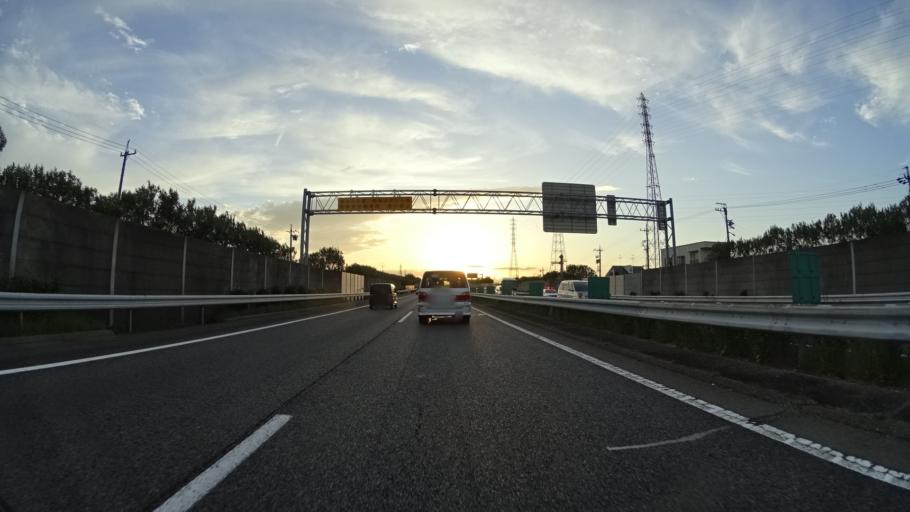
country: JP
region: Aichi
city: Ichinomiya
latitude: 35.2782
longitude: 136.8043
